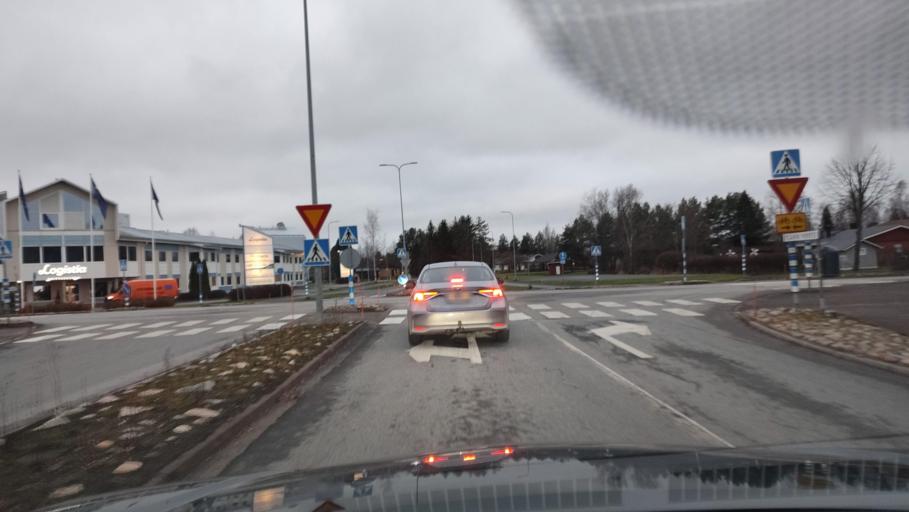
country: FI
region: Southern Ostrobothnia
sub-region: Suupohja
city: Kauhajoki
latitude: 62.4177
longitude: 22.1758
